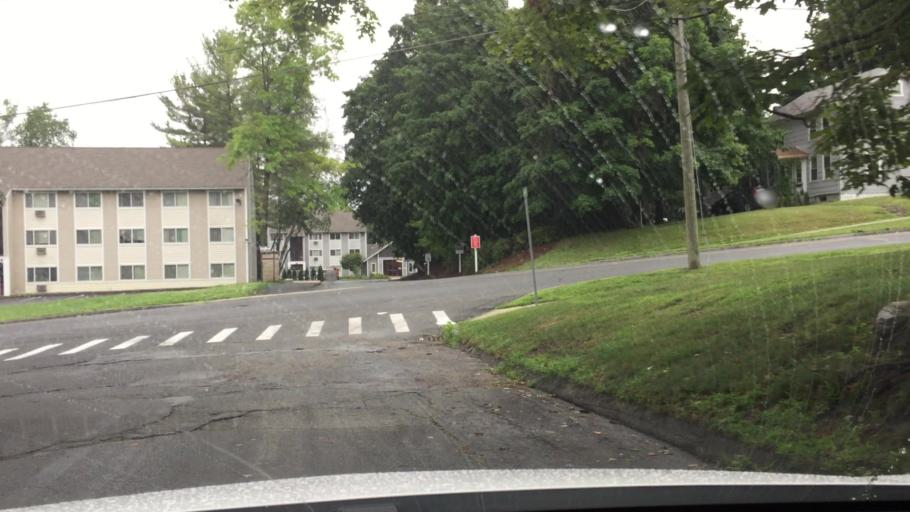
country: US
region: Massachusetts
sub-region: Berkshire County
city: Pittsfield
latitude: 42.4504
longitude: -73.2639
